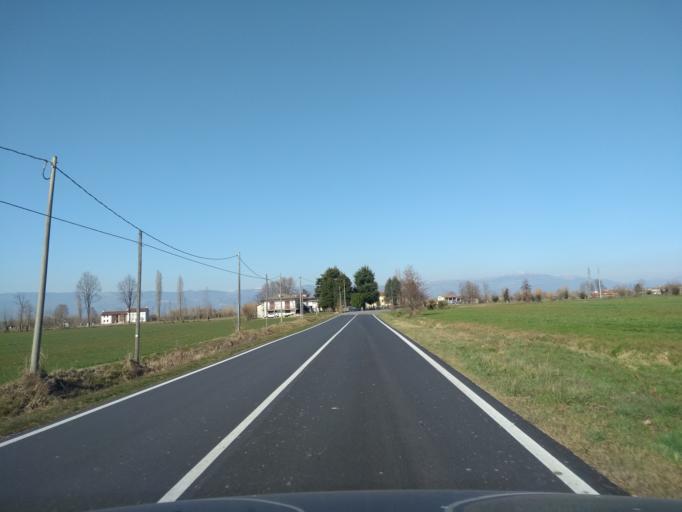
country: IT
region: Veneto
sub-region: Provincia di Vicenza
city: Bolzano Vicentino
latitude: 45.6043
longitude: 11.6447
